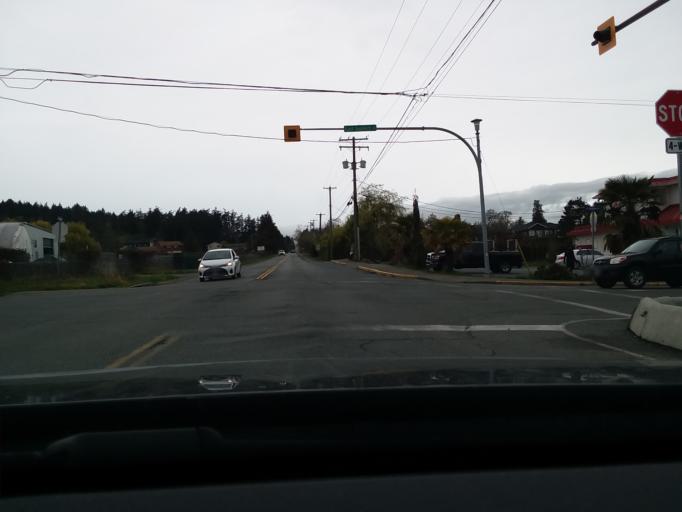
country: CA
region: British Columbia
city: North Saanich
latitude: 48.6300
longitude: -123.4202
